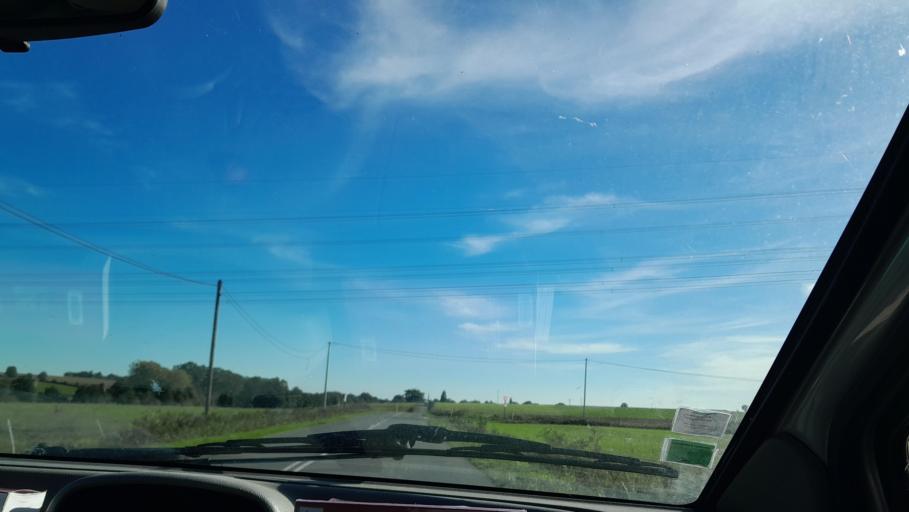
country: FR
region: Brittany
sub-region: Departement d'Ille-et-Vilaine
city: Argentre-du-Plessis
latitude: 48.0026
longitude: -1.1293
